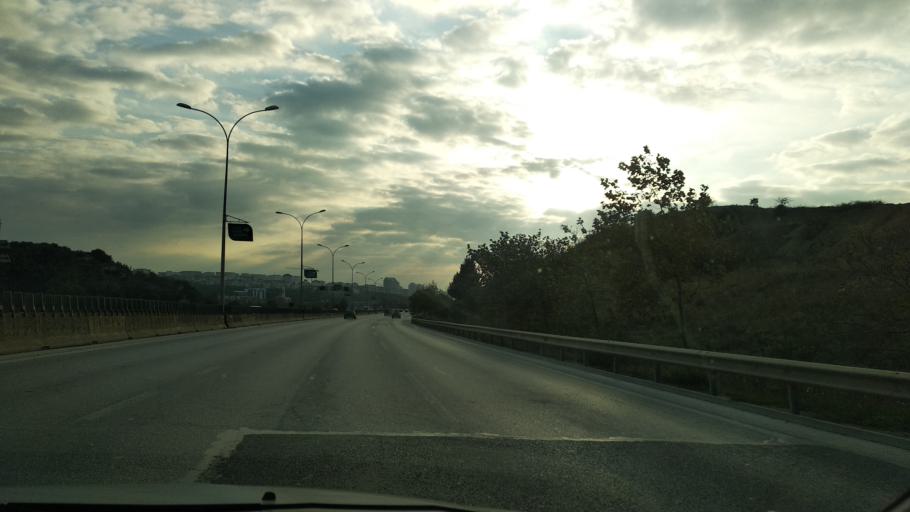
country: TR
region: Istanbul
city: Icmeler
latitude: 40.8848
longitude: 29.3215
